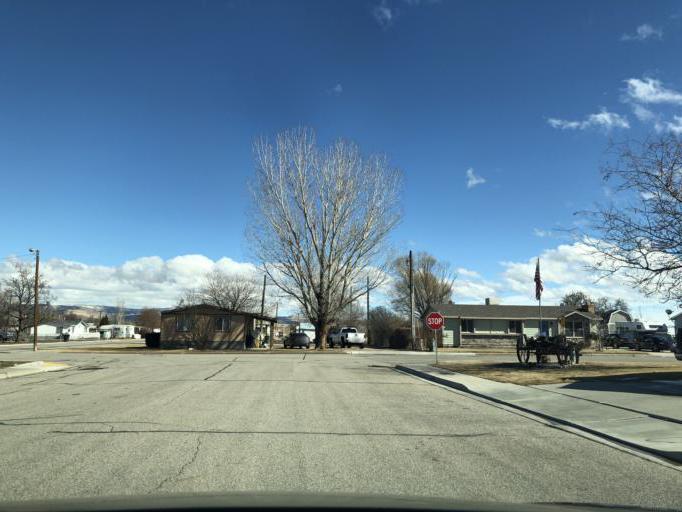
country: US
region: Utah
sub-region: Carbon County
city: East Carbon City
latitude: 38.9993
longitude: -110.1603
